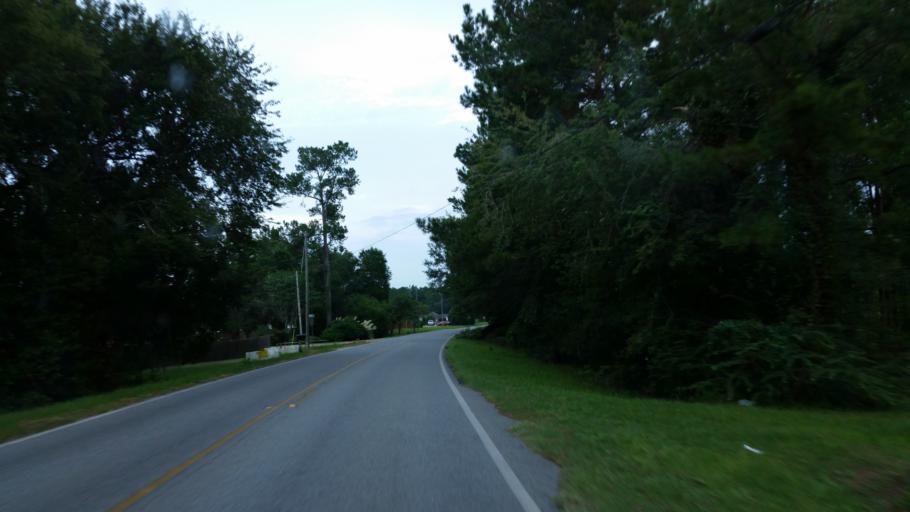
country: US
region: Georgia
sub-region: Lowndes County
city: Valdosta
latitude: 30.7590
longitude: -83.2601
